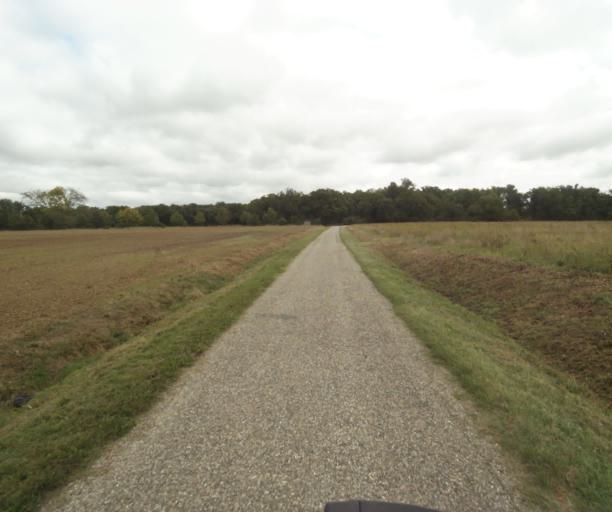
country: FR
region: Midi-Pyrenees
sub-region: Departement du Tarn-et-Garonne
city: Montech
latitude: 43.9587
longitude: 1.2562
